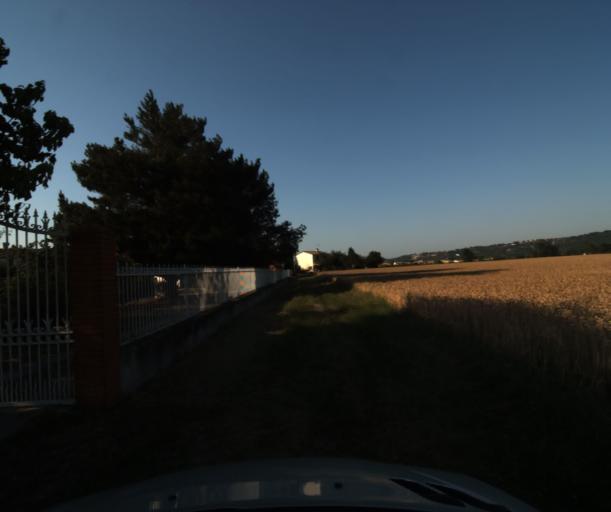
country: FR
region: Midi-Pyrenees
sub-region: Departement de la Haute-Garonne
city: Roquettes
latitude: 43.4809
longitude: 1.3889
